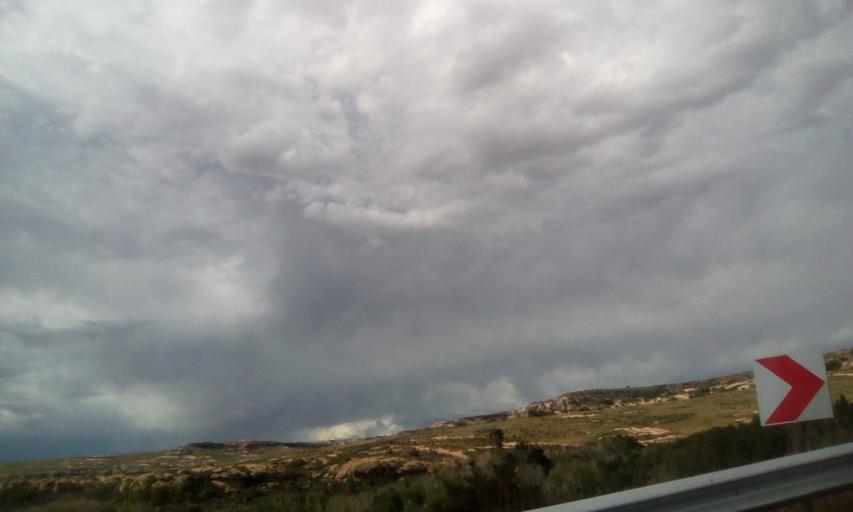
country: ZA
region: Orange Free State
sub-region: Thabo Mofutsanyana District Municipality
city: Ladybrand
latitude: -29.2495
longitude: 27.4354
